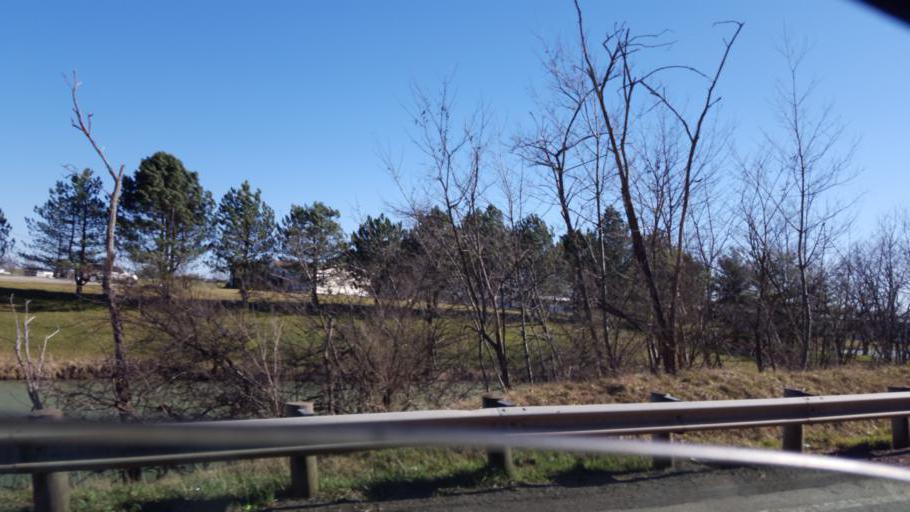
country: US
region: Ohio
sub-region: Wayne County
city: Dalton
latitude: 40.6866
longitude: -81.7103
